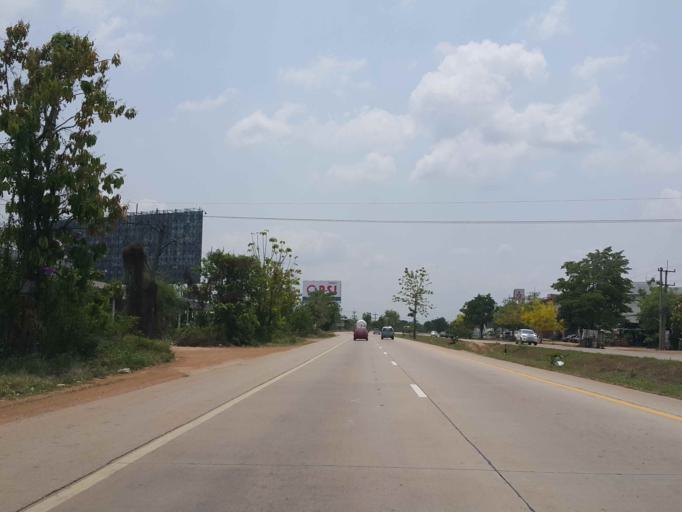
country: TH
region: Lampang
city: Ko Kha
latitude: 18.2169
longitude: 99.4234
